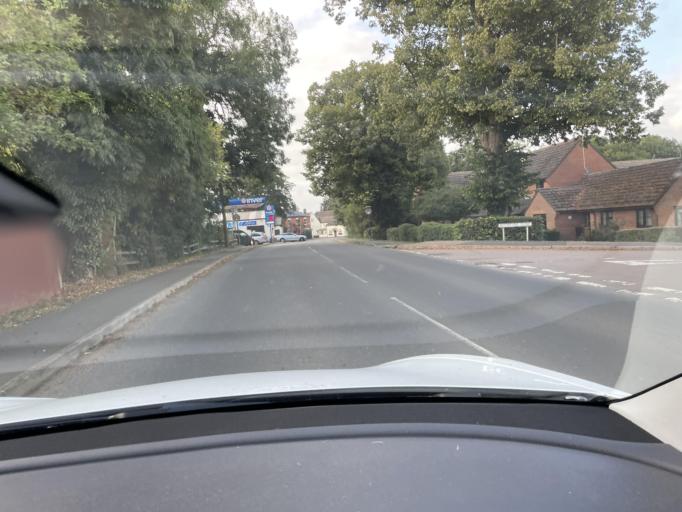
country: GB
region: England
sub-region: Northamptonshire
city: Long Buckby
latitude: 52.4151
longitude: -1.0578
